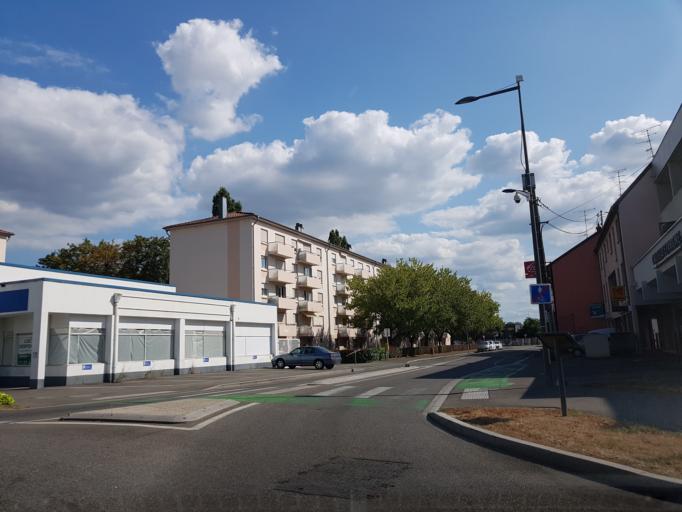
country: FR
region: Alsace
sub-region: Departement du Haut-Rhin
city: Illzach
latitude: 47.7792
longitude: 7.3473
